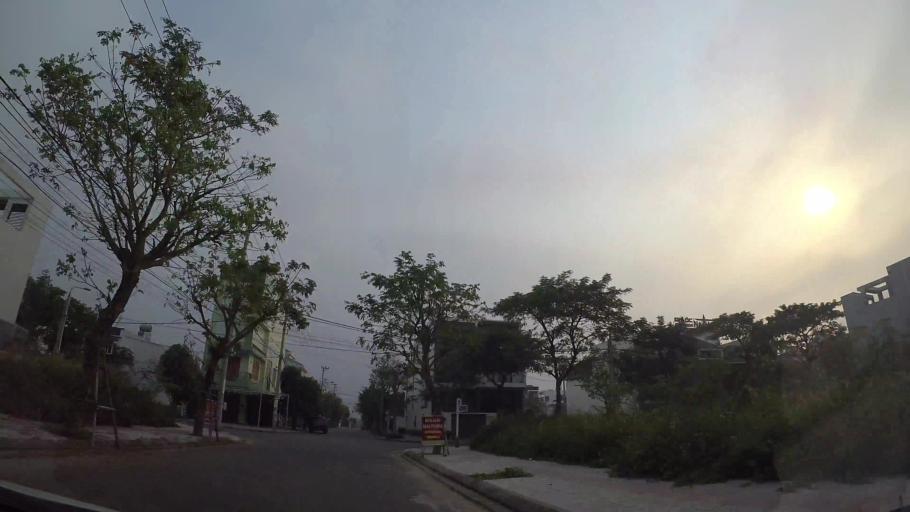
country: VN
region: Da Nang
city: Cam Le
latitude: 16.0215
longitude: 108.2278
